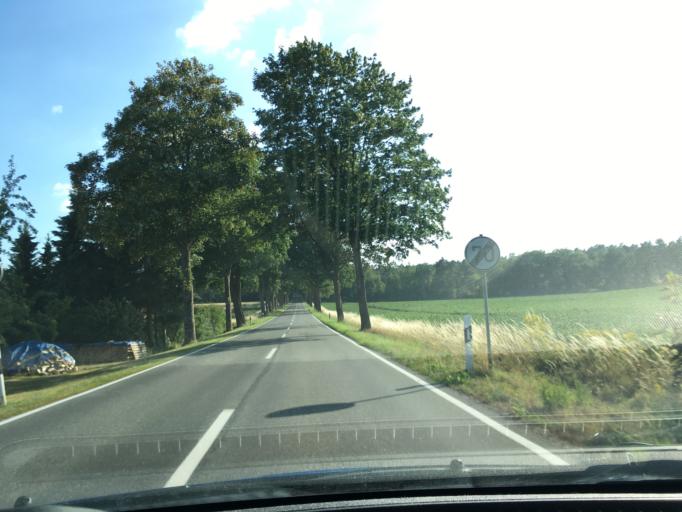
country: DE
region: Lower Saxony
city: Dahlenburg
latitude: 53.1670
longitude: 10.6976
